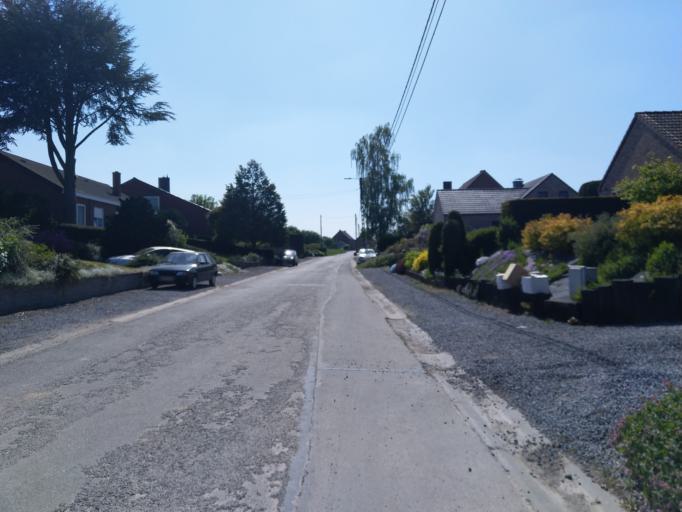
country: BE
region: Wallonia
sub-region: Province du Hainaut
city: Soignies
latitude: 50.5633
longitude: 4.0074
